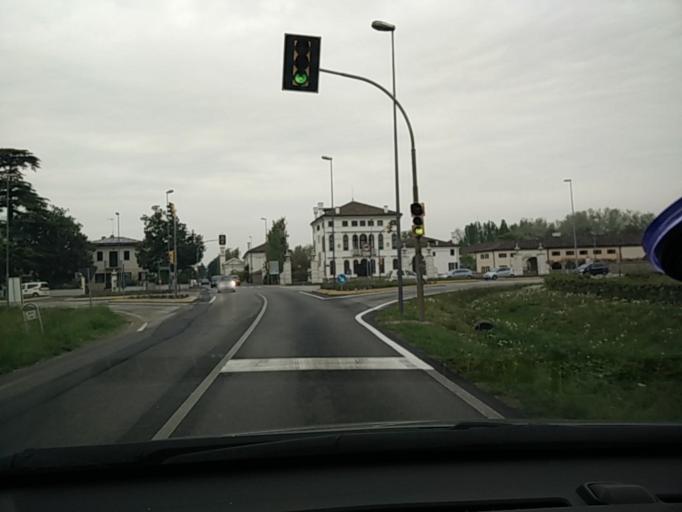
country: IT
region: Veneto
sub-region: Provincia di Treviso
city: Ponzano
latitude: 45.7075
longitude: 12.2181
